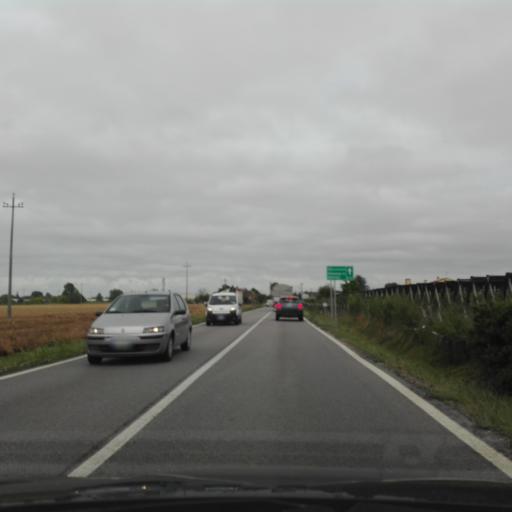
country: IT
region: Veneto
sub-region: Provincia di Rovigo
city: Villanova del Ghebbo Canton
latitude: 45.0769
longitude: 11.6334
